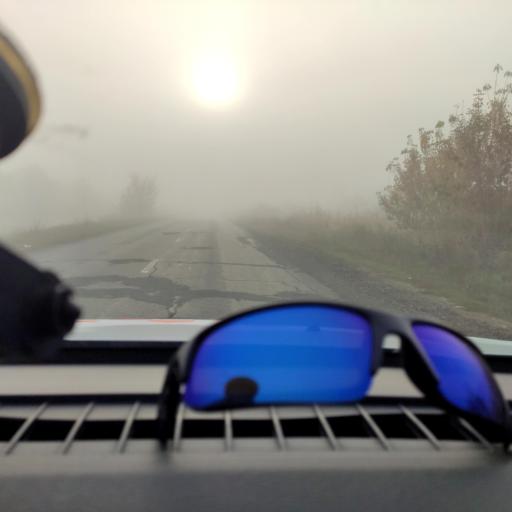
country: RU
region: Samara
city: Chapayevsk
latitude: 53.0045
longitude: 49.7470
